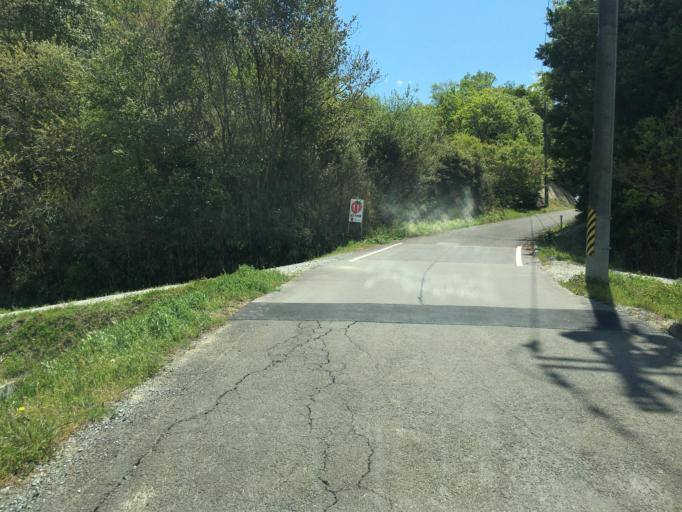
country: JP
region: Miyagi
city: Marumori
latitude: 37.8110
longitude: 140.9492
